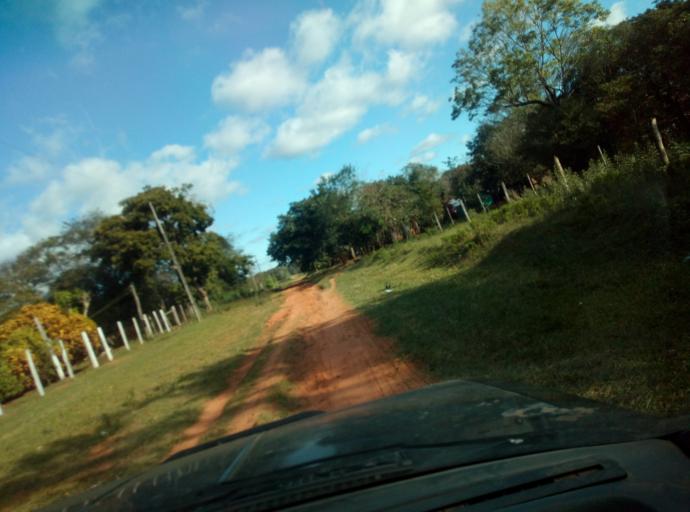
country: PY
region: Caaguazu
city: Doctor Cecilio Baez
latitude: -25.1639
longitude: -56.2724
